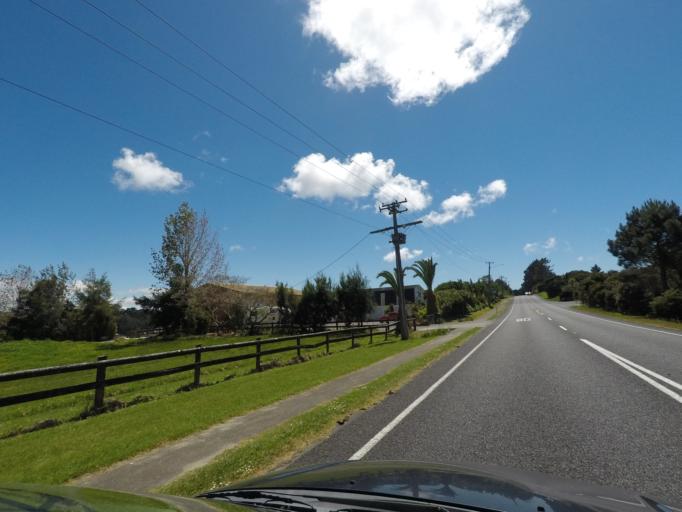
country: NZ
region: Auckland
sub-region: Auckland
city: Rothesay Bay
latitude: -36.7491
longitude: 174.6703
